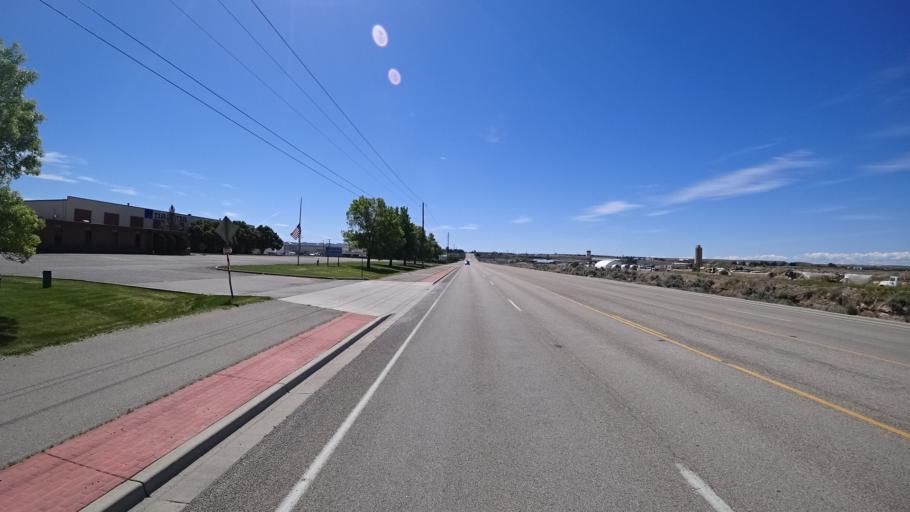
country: US
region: Idaho
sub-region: Ada County
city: Boise
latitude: 43.5553
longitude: -116.1627
